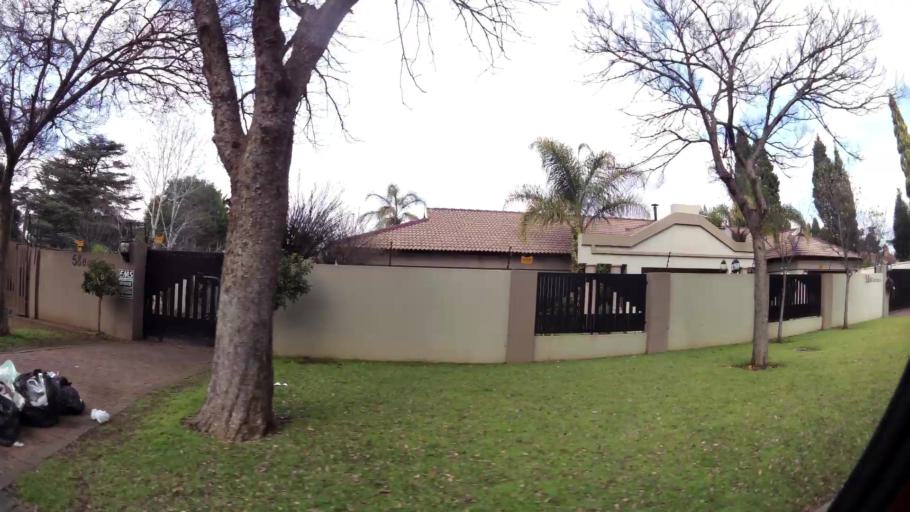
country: ZA
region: Gauteng
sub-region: Sedibeng District Municipality
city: Vanderbijlpark
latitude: -26.7417
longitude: 27.8342
